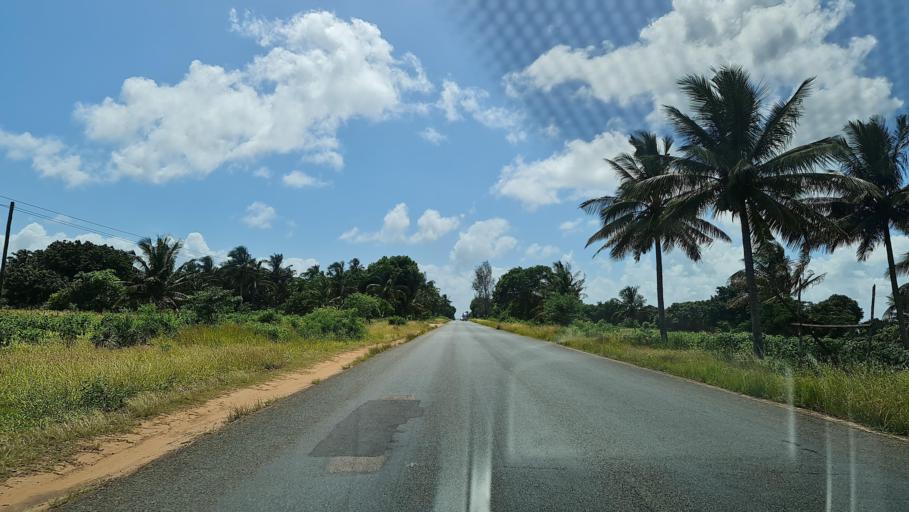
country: MZ
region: Inhambane
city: Maxixe
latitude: -24.5279
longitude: 34.9543
